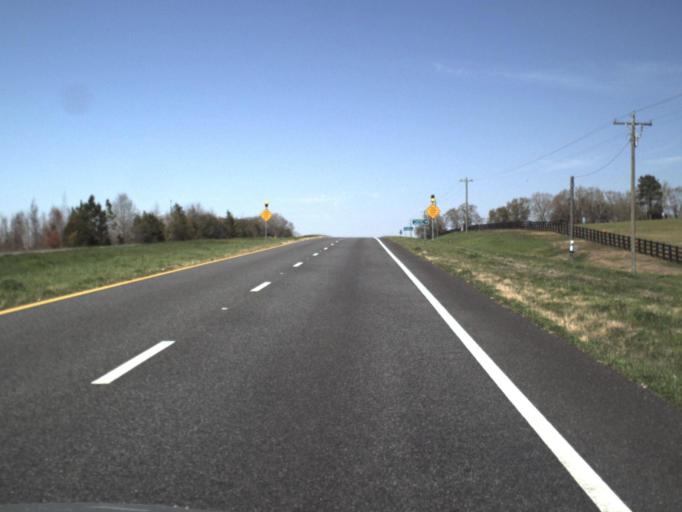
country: US
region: Florida
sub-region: Jackson County
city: Graceville
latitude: 30.8835
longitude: -85.3658
